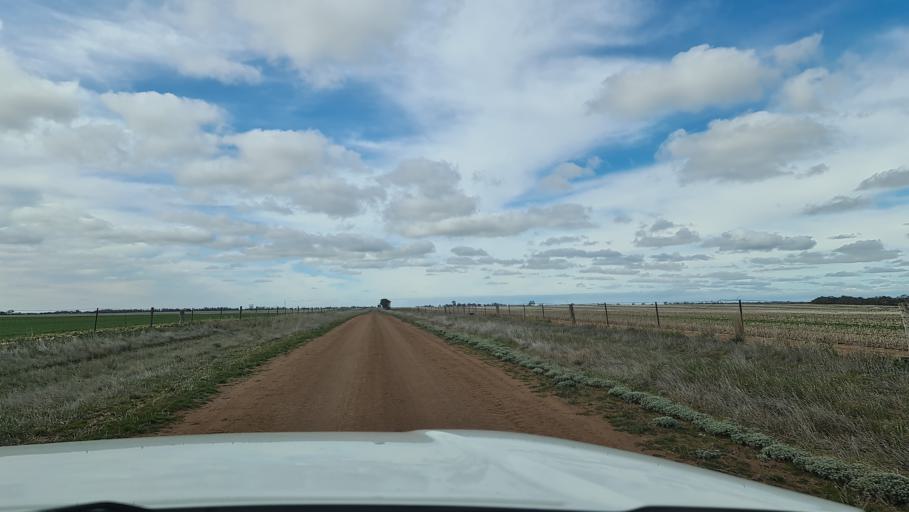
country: AU
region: Victoria
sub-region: Horsham
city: Horsham
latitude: -36.6312
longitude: 142.4204
